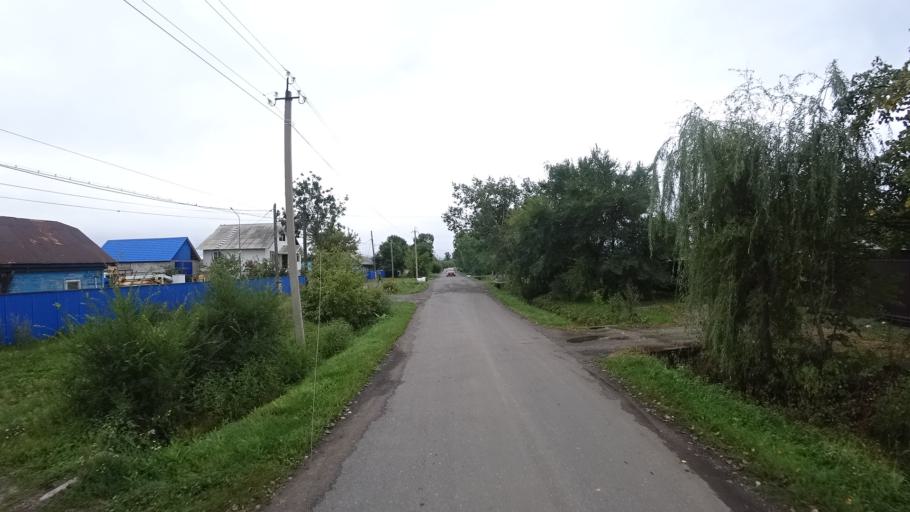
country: RU
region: Primorskiy
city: Chernigovka
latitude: 44.3443
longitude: 132.5829
